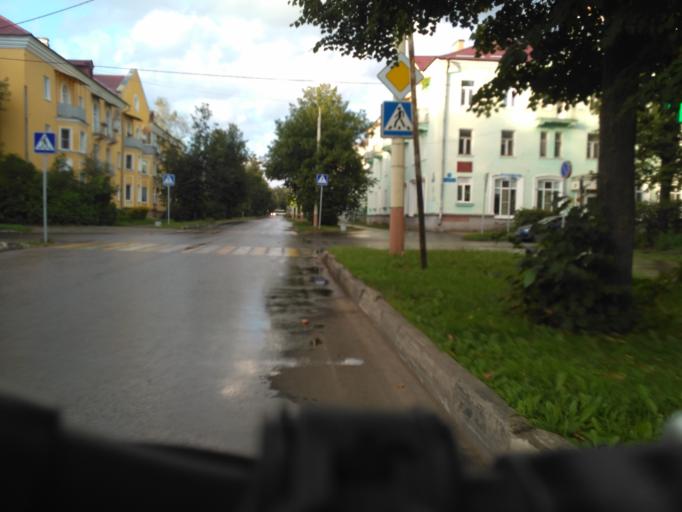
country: RU
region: Moskovskaya
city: Dubna
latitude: 56.7469
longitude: 37.1989
